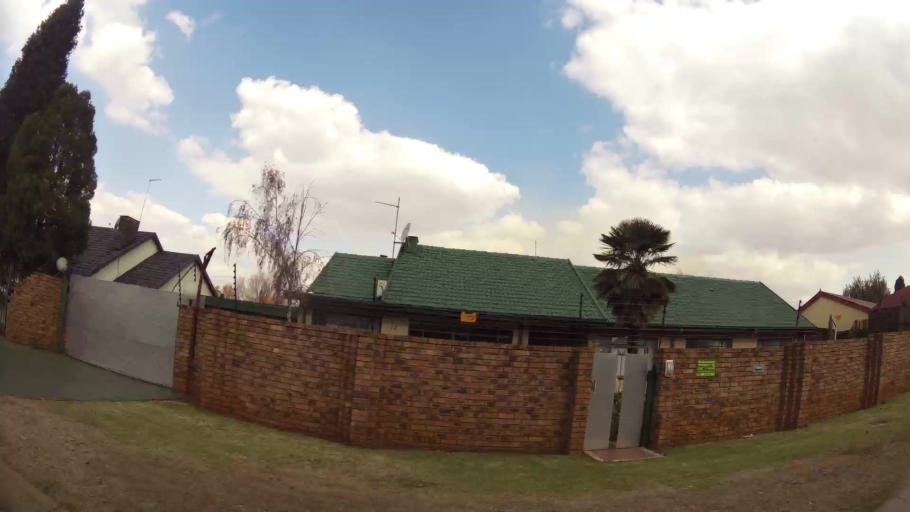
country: ZA
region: Mpumalanga
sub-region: Nkangala District Municipality
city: Delmas
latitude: -26.1426
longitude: 28.6719
